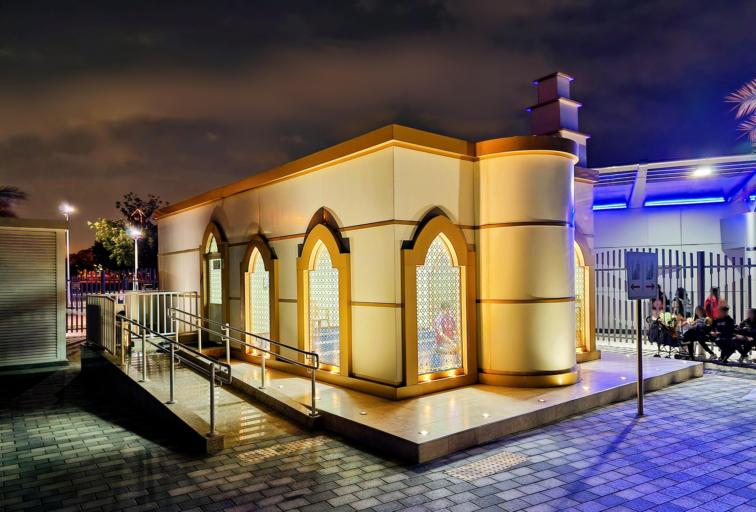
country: AE
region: Ash Shariqah
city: Sharjah
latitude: 25.2346
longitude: 55.3011
